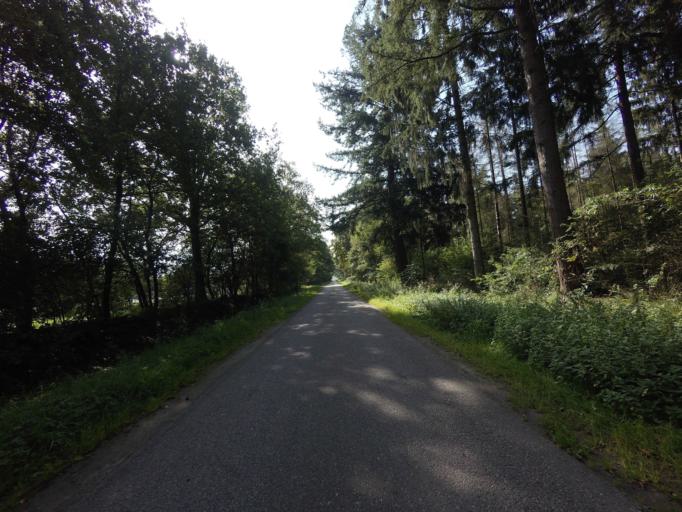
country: NL
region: Drenthe
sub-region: Gemeente Borger-Odoorn
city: Borger
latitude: 52.9391
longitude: 6.6967
